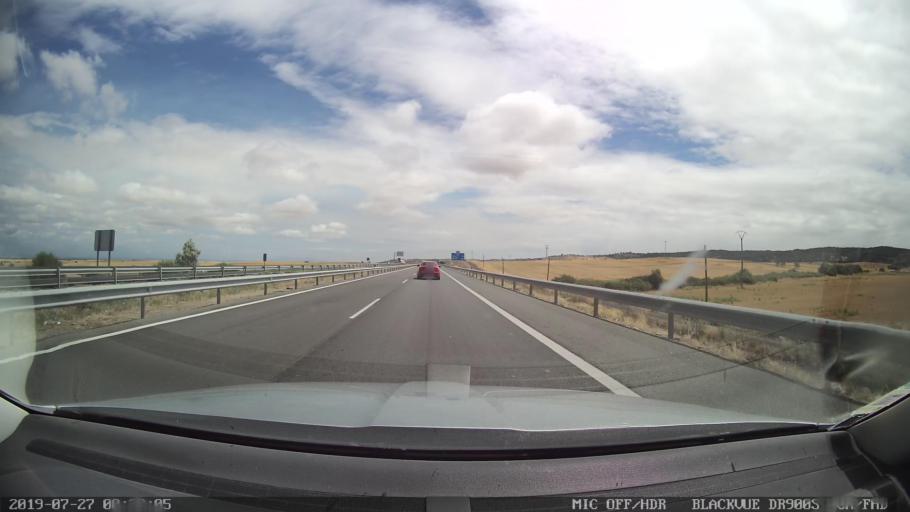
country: ES
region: Castille-La Mancha
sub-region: Province of Toledo
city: Herreruela de Oropesa
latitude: 39.9033
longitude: -5.2392
